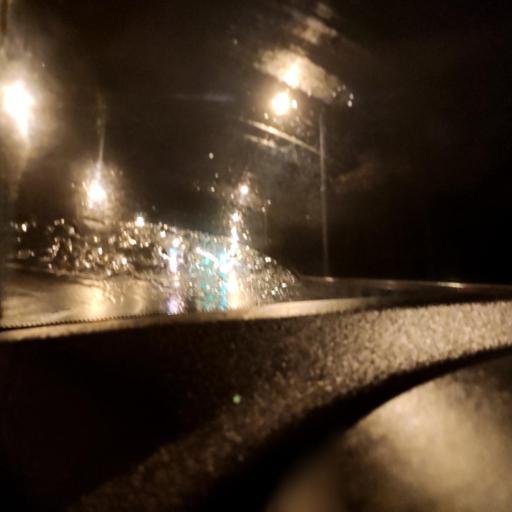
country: RU
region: Samara
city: Petra-Dubrava
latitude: 53.3048
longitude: 50.2401
